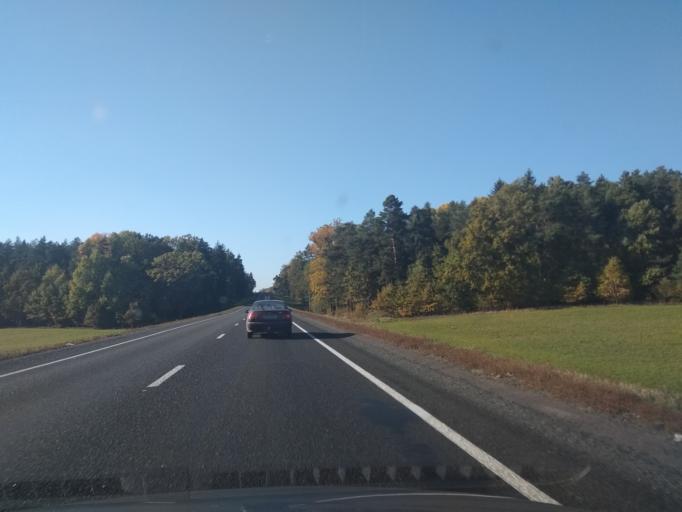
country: BY
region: Grodnenskaya
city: Slonim
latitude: 53.0551
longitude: 25.3151
